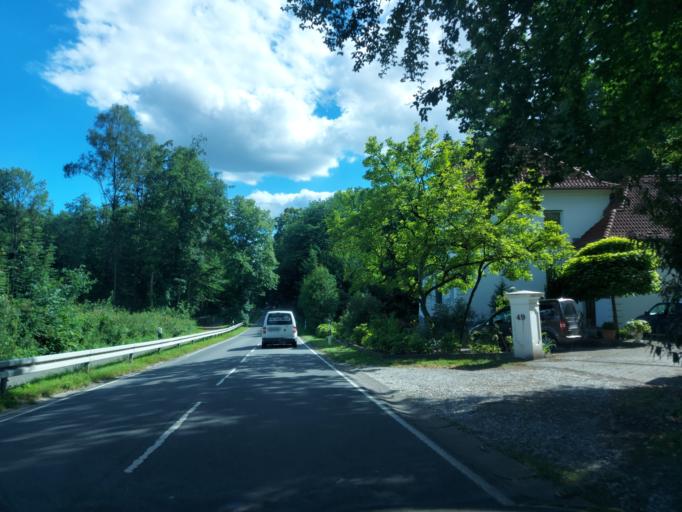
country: DE
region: Lower Saxony
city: Bad Iburg
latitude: 52.1685
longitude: 8.0423
